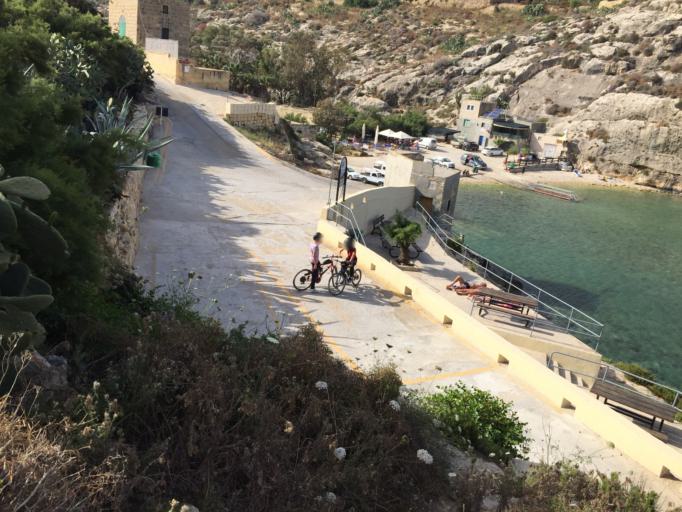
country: MT
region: Ghajnsielem
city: Ghajnsielem
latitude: 36.0196
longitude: 14.2712
